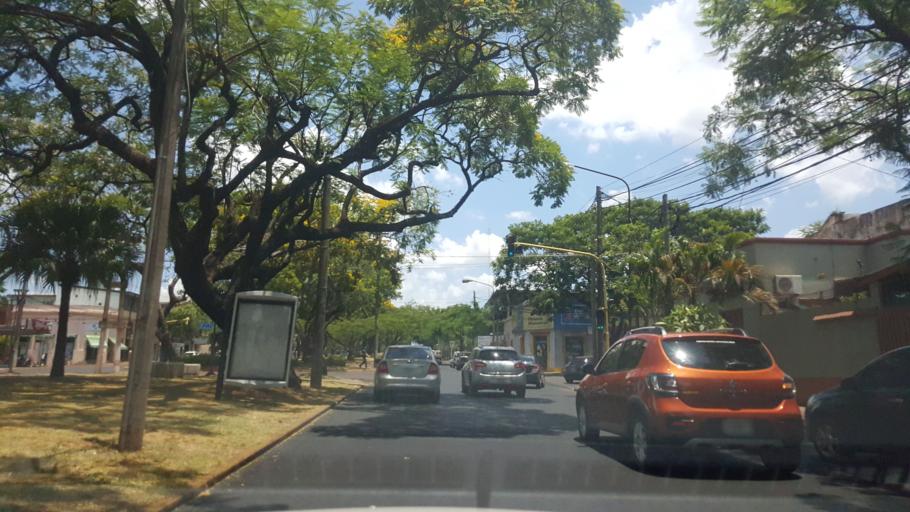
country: AR
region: Misiones
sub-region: Departamento de Capital
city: Posadas
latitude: -27.3700
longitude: -55.9018
